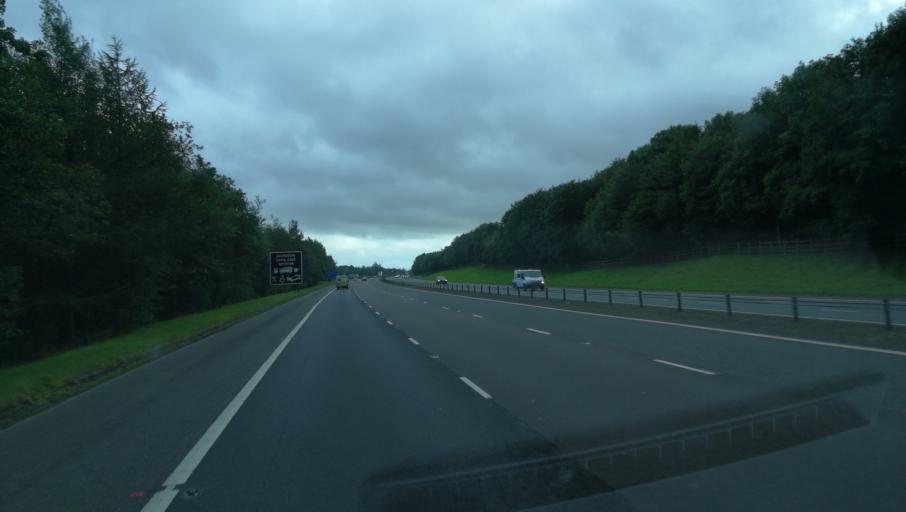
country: GB
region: Scotland
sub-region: Dumfries and Galloway
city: Moffat
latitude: 55.2503
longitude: -3.4097
